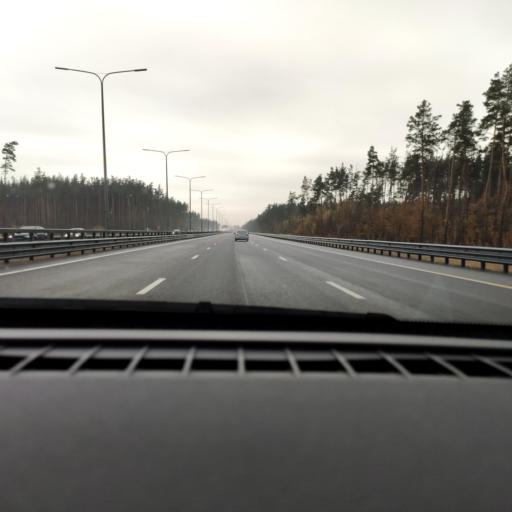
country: RU
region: Voronezj
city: Somovo
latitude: 51.7086
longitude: 39.3066
